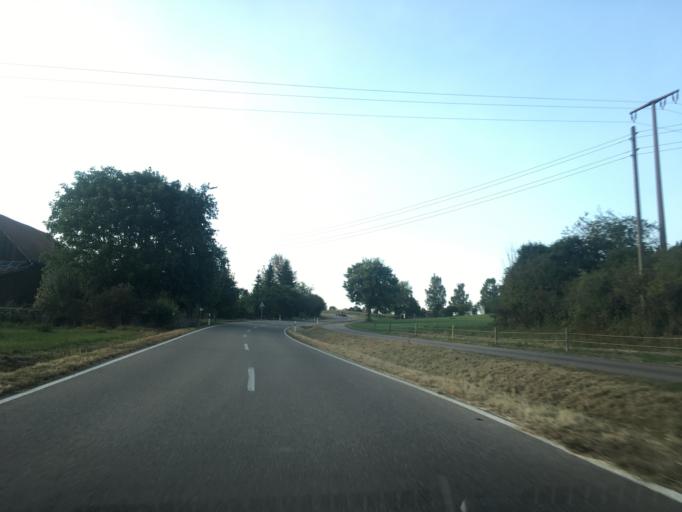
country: DE
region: Baden-Wuerttemberg
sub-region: Tuebingen Region
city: Rechtenstein
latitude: 48.2430
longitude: 9.5491
